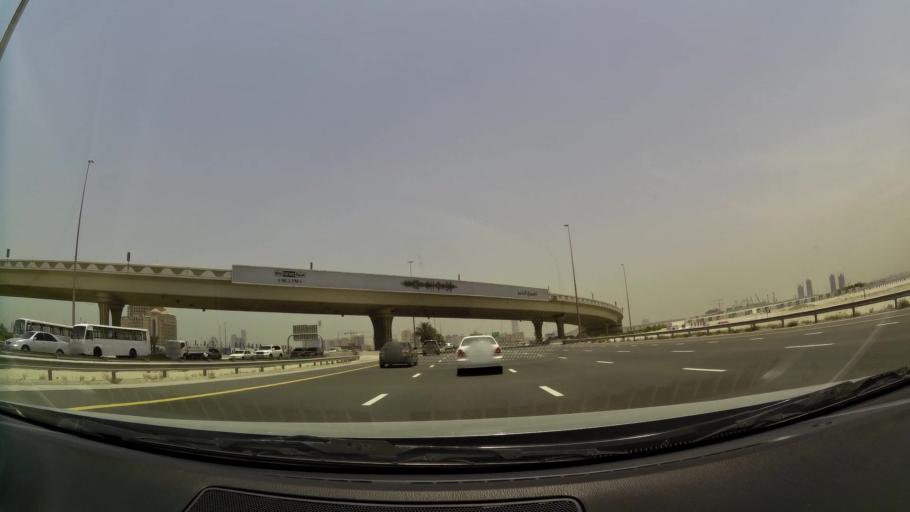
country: AE
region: Ash Shariqah
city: Sharjah
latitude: 25.2064
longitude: 55.3154
